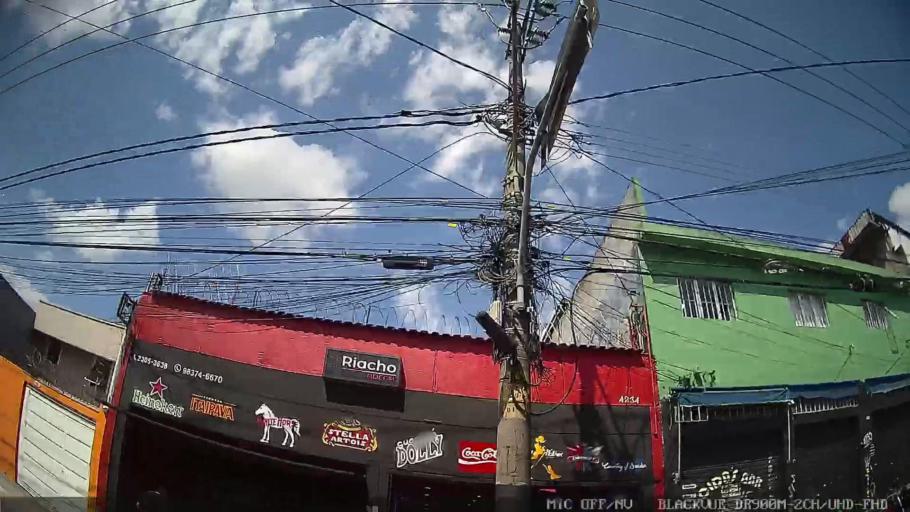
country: BR
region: Sao Paulo
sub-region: Guarulhos
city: Guarulhos
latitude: -23.5090
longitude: -46.4776
